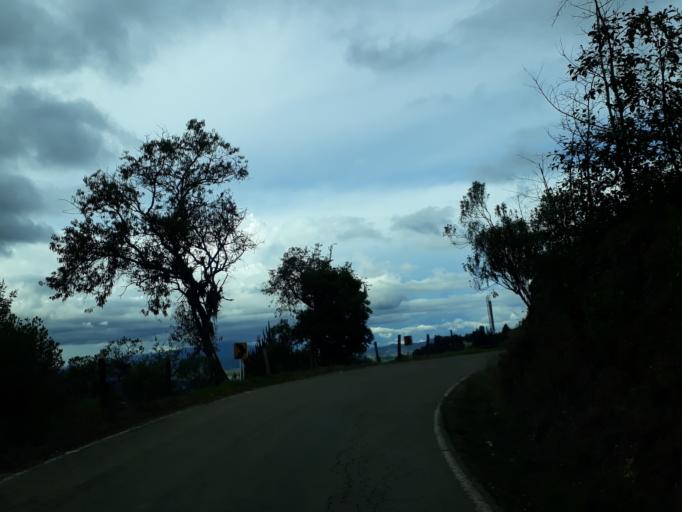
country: CO
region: Cundinamarca
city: Susa
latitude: 5.3975
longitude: -73.7878
